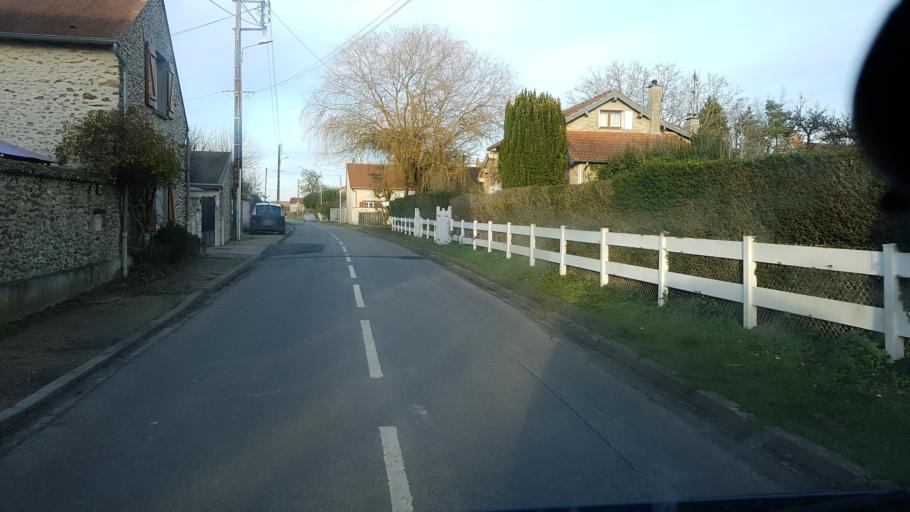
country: FR
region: Ile-de-France
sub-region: Departement des Yvelines
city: Le Perray-en-Yvelines
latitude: 48.7029
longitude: 1.8109
